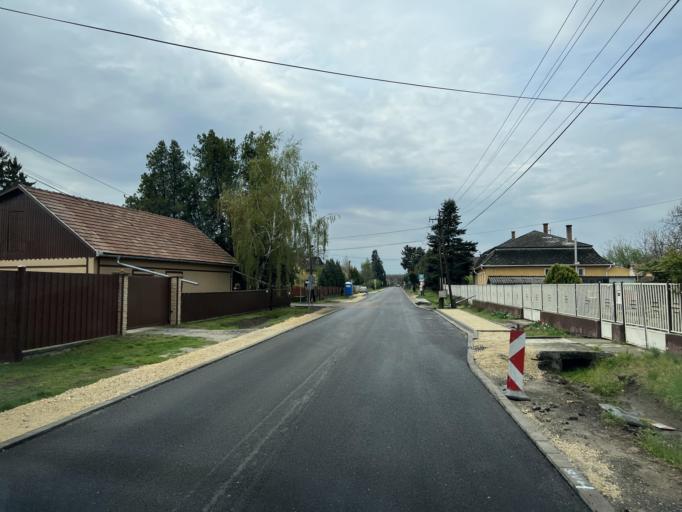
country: HU
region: Pest
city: Danszentmiklos
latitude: 47.2071
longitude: 19.5653
